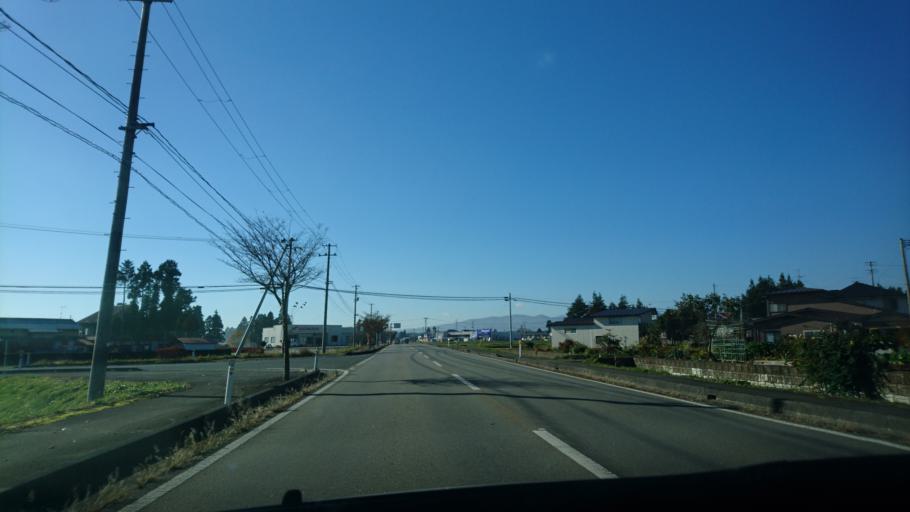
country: JP
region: Iwate
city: Mizusawa
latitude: 39.1341
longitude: 141.0675
